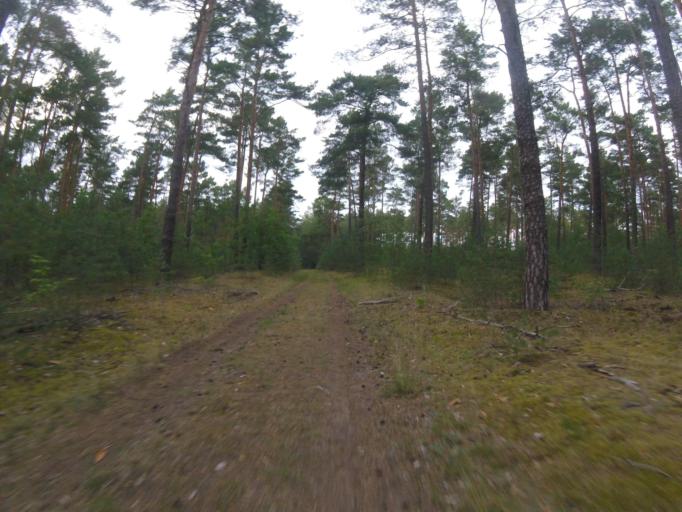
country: DE
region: Brandenburg
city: Gross Koris
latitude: 52.1592
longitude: 13.6808
